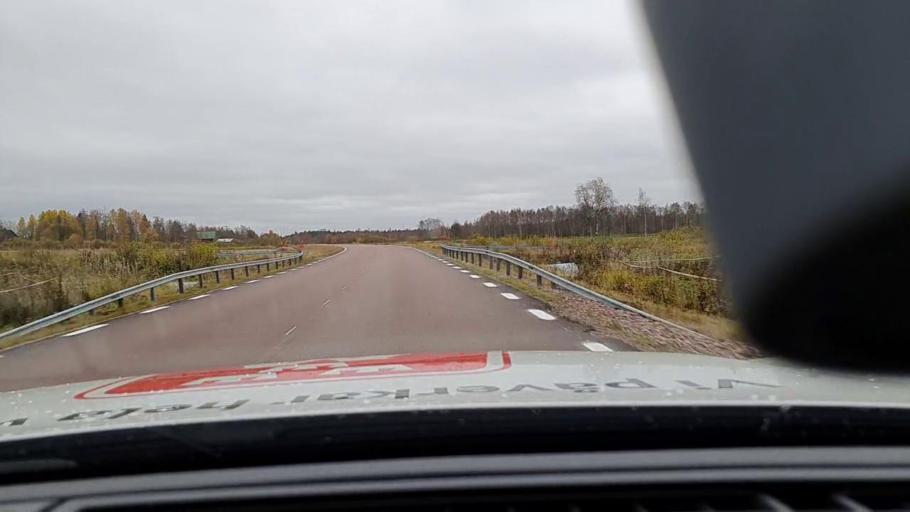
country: FI
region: Lapland
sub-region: Kemi-Tornio
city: Tornio
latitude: 66.0614
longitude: 23.9259
